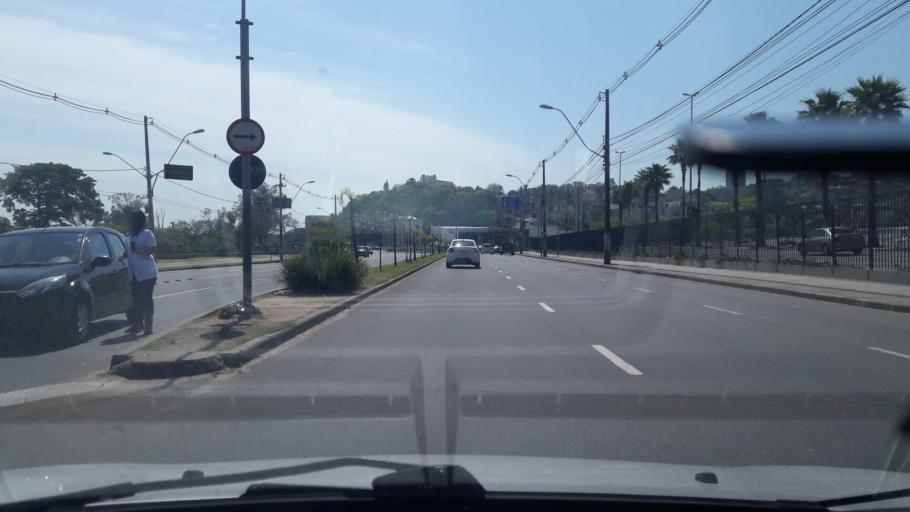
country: BR
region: Rio Grande do Sul
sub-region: Porto Alegre
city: Porto Alegre
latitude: -30.0828
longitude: -51.2468
